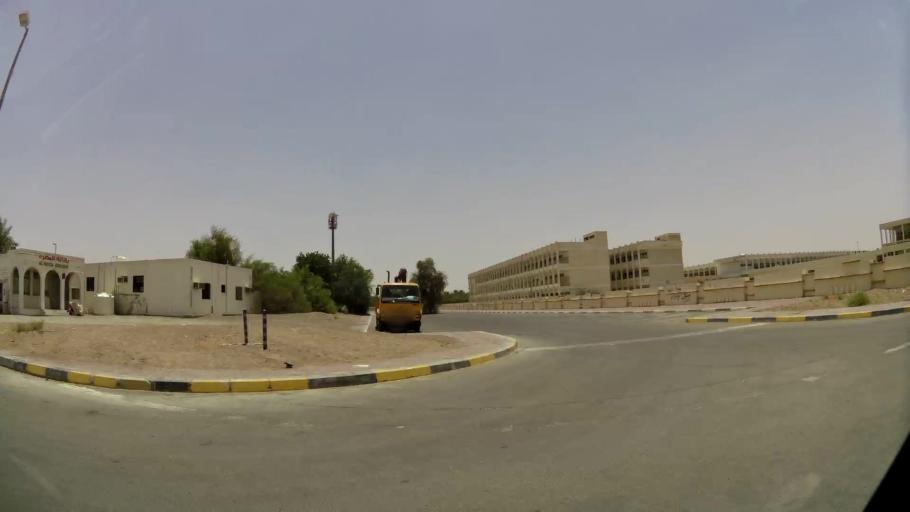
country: AE
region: Abu Dhabi
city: Al Ain
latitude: 24.2183
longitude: 55.7160
